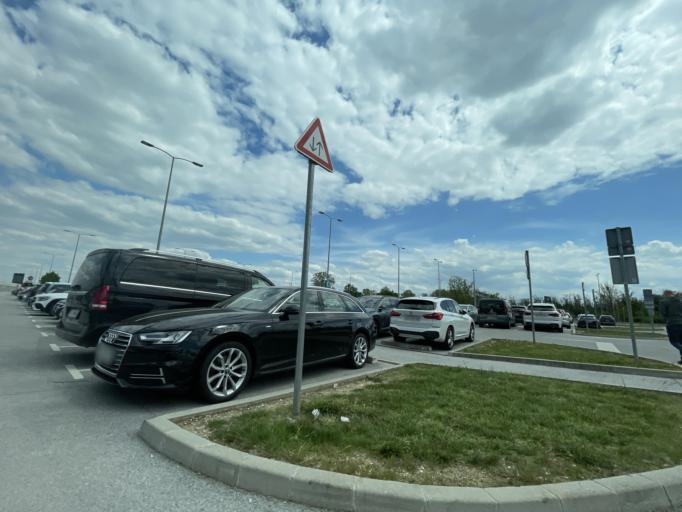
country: HR
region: Zagrebacka
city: Micevec
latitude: 45.7408
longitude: 16.0820
